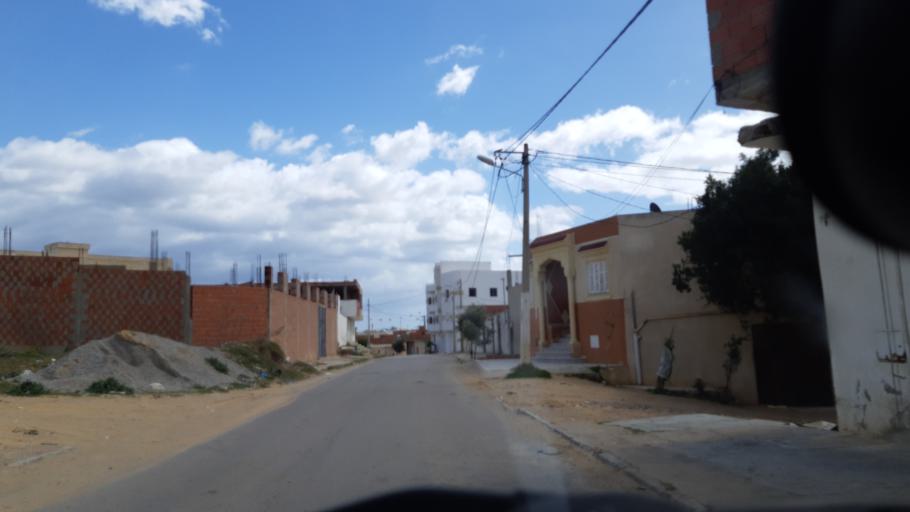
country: TN
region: Susah
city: Akouda
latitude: 35.8765
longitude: 10.5183
